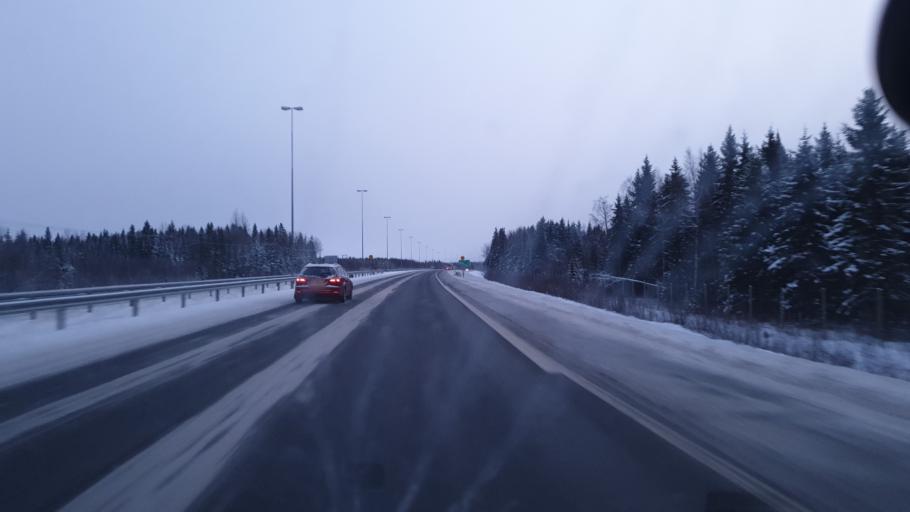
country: FI
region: Lapland
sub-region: Kemi-Tornio
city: Tornio
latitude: 65.8385
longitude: 24.2979
